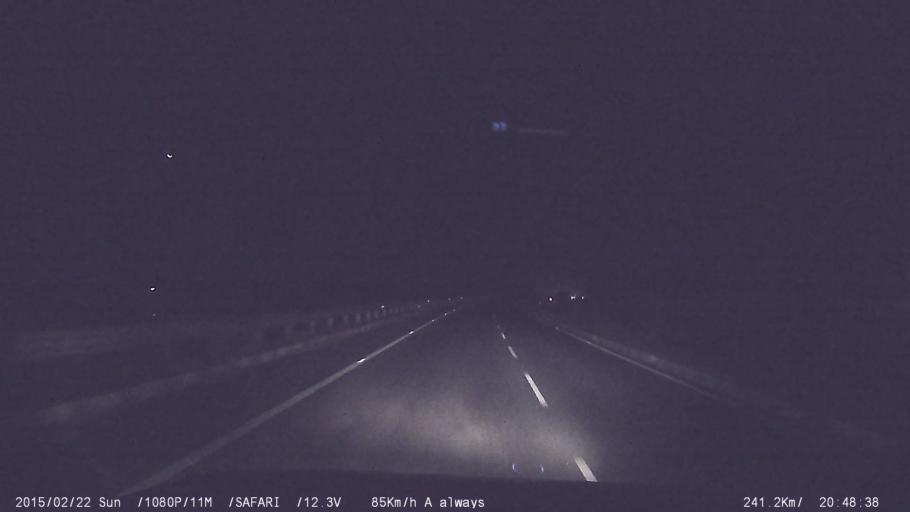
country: IN
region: Tamil Nadu
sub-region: Dindigul
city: Vedasandur
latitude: 10.5087
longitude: 77.9393
